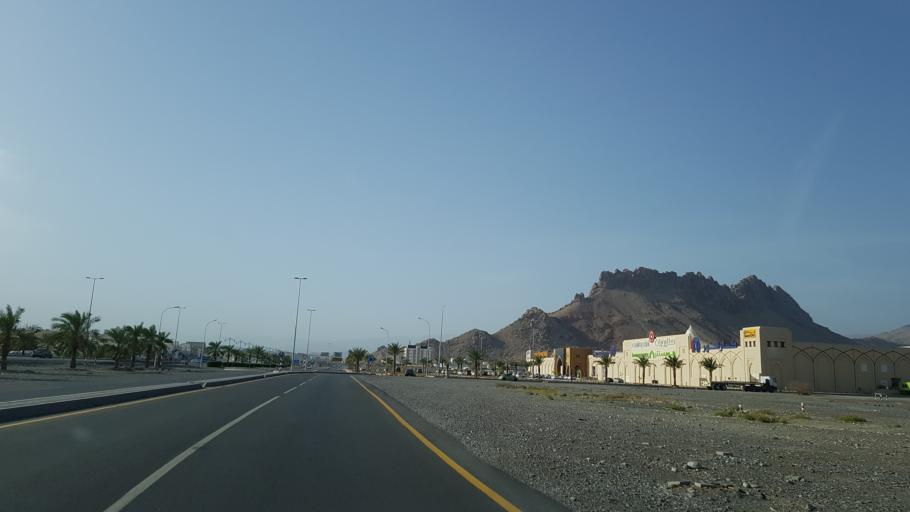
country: OM
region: Muhafazat ad Dakhiliyah
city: Nizwa
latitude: 22.8686
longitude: 57.5373
